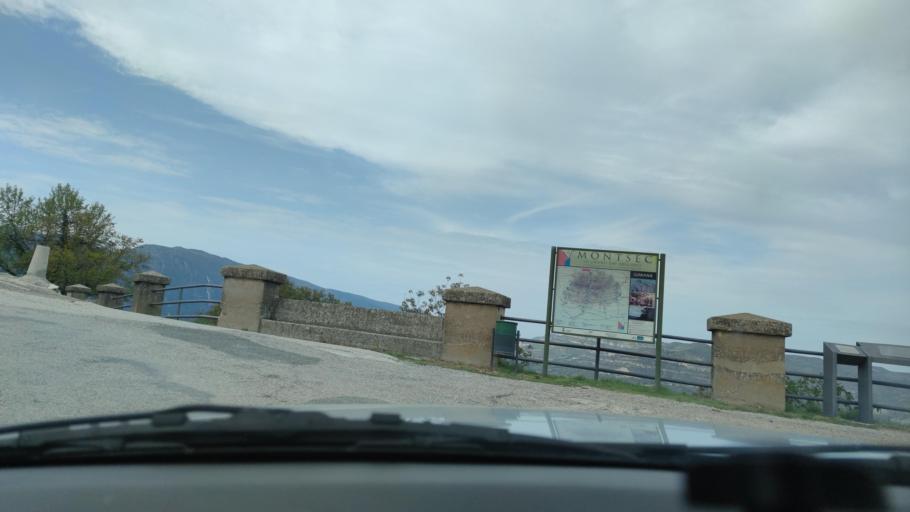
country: ES
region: Catalonia
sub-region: Provincia de Lleida
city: Llimiana
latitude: 42.0766
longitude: 0.9162
